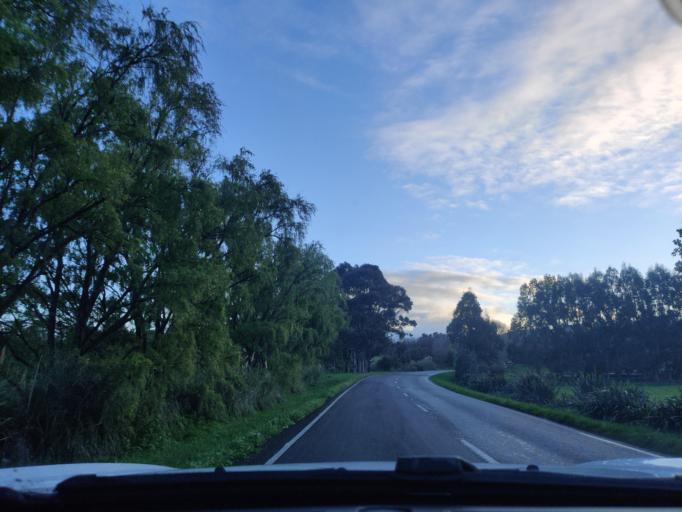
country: NZ
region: Manawatu-Wanganui
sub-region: Palmerston North City
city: Palmerston North
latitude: -40.3154
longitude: 175.7557
